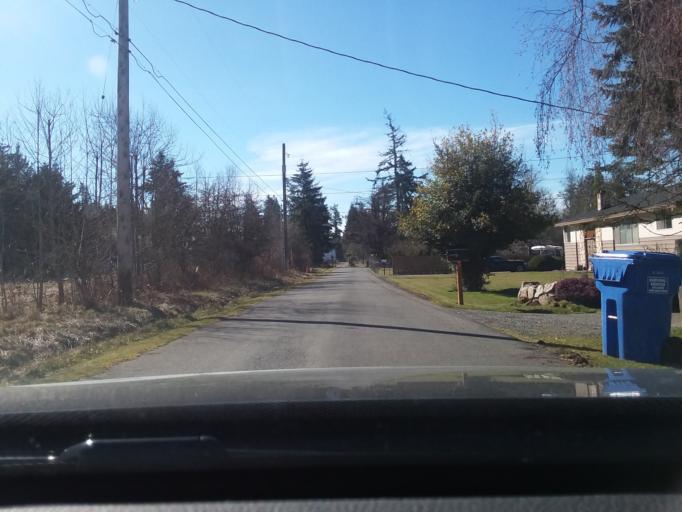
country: US
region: Washington
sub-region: Pierce County
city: Waller
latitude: 47.1821
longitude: -122.3838
